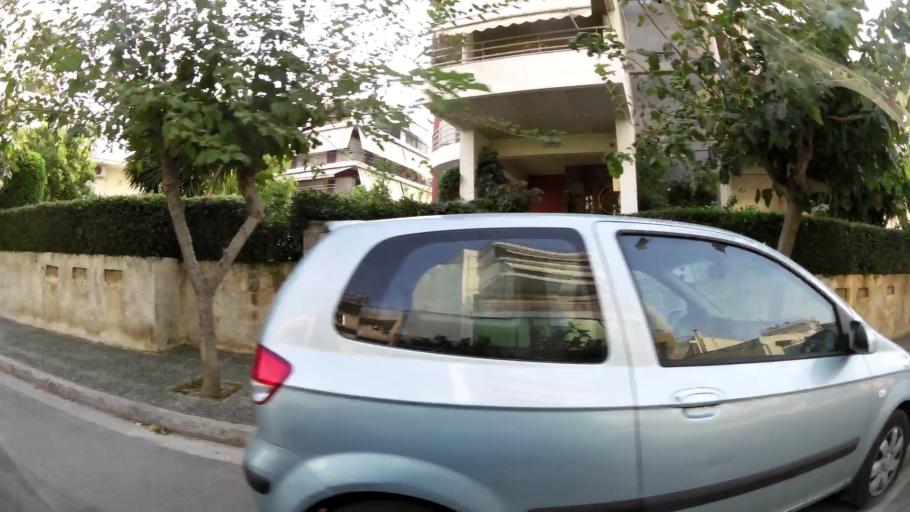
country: GR
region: Attica
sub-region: Nomarchia Athinas
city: Agios Dimitrios
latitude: 37.9300
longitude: 23.7238
